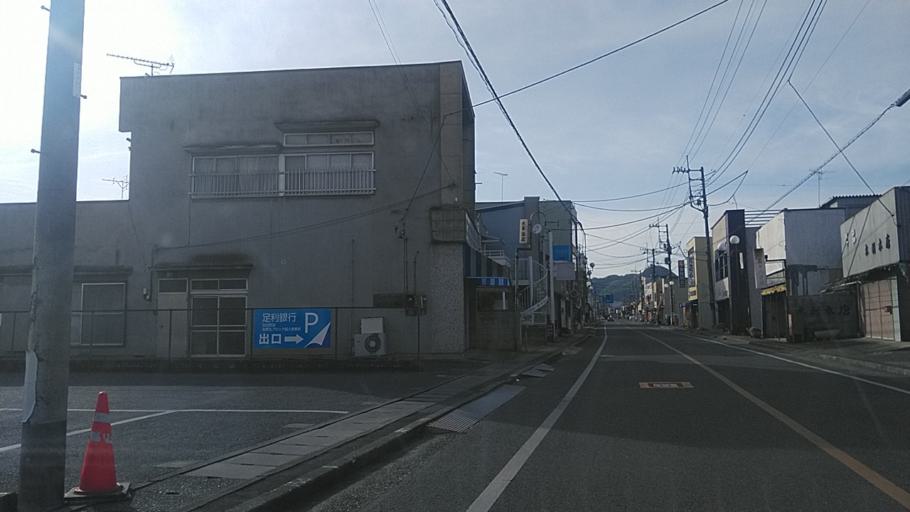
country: JP
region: Tochigi
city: Tanuma
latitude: 36.3675
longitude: 139.5790
